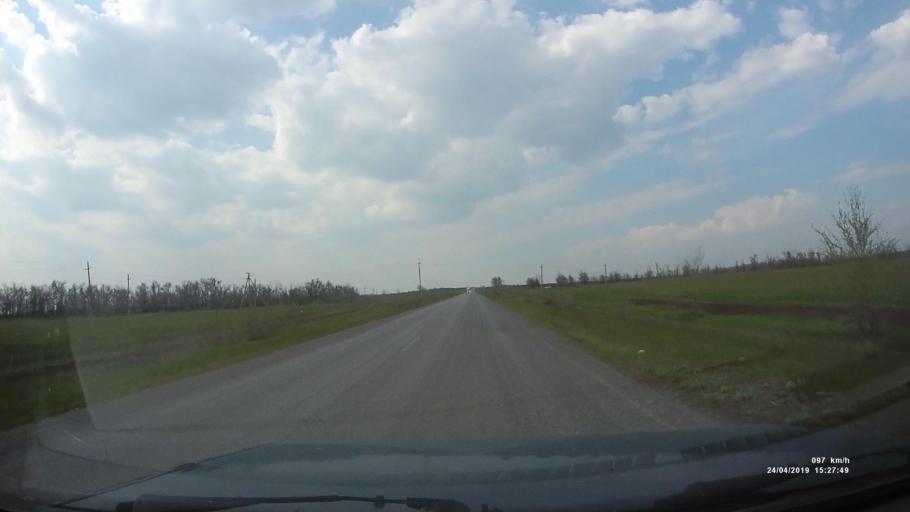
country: RU
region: Rostov
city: Remontnoye
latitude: 46.5702
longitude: 43.0231
